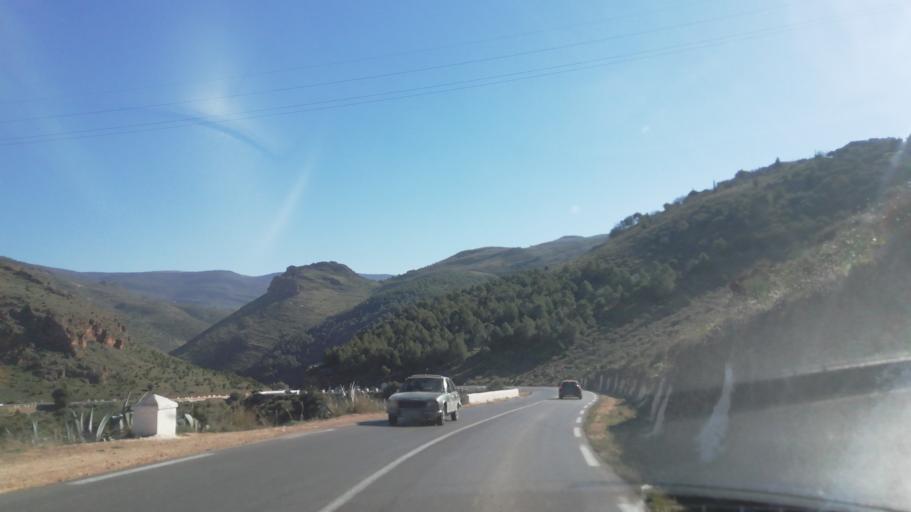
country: DZ
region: Tlemcen
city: Beni Mester
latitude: 34.8403
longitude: -1.4673
